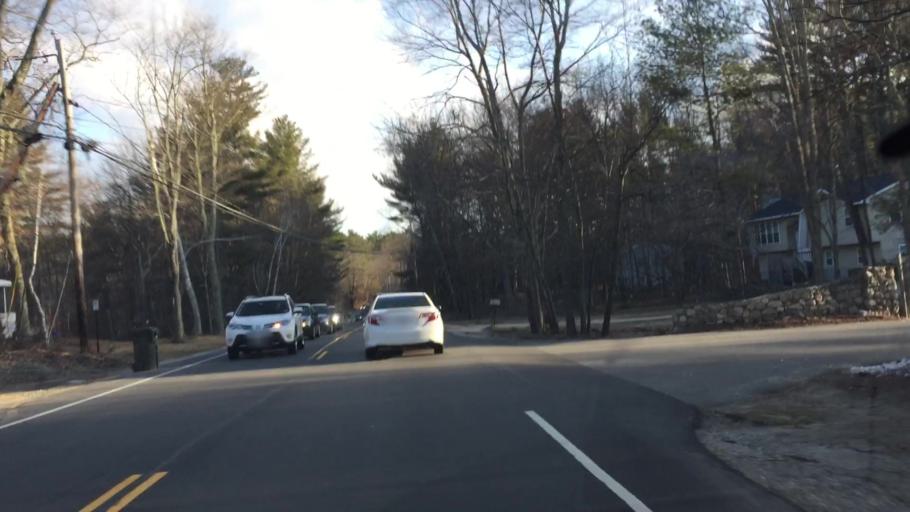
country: US
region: New Hampshire
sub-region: Rockingham County
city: Londonderry
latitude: 42.8273
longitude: -71.3654
